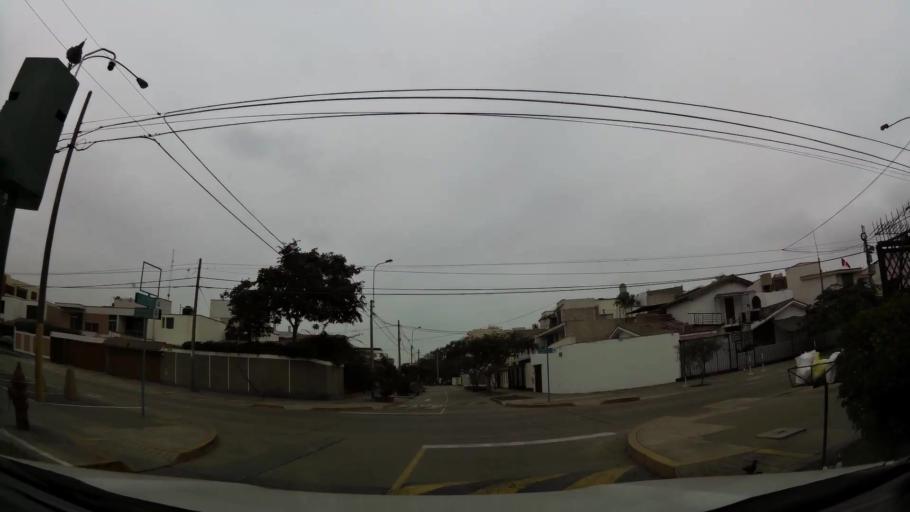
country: PE
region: Lima
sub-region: Lima
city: San Luis
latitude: -12.0974
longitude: -77.0071
